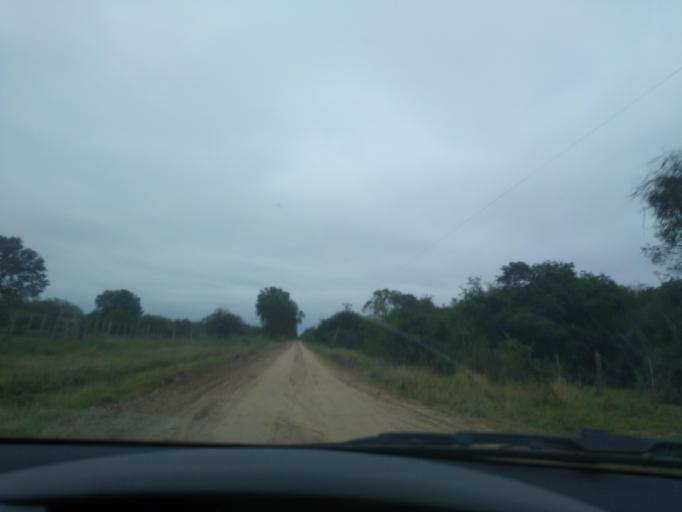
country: AR
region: Chaco
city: Colonia Benitez
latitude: -27.3587
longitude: -58.9612
